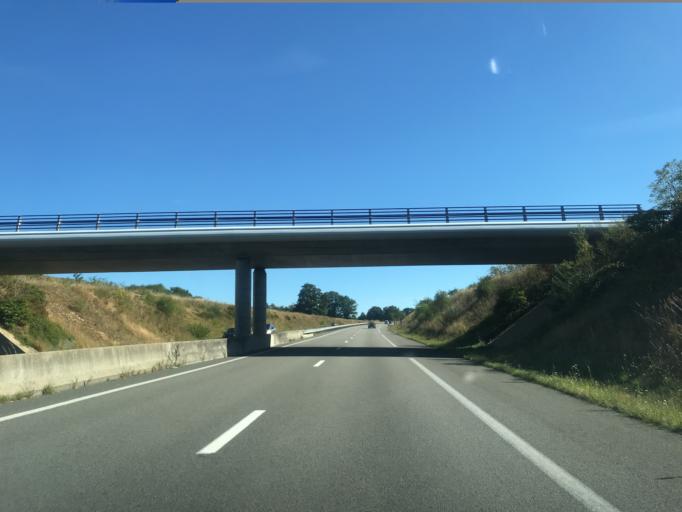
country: FR
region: Limousin
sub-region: Departement de la Creuse
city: Gouzon
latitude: 46.2232
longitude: 2.3003
